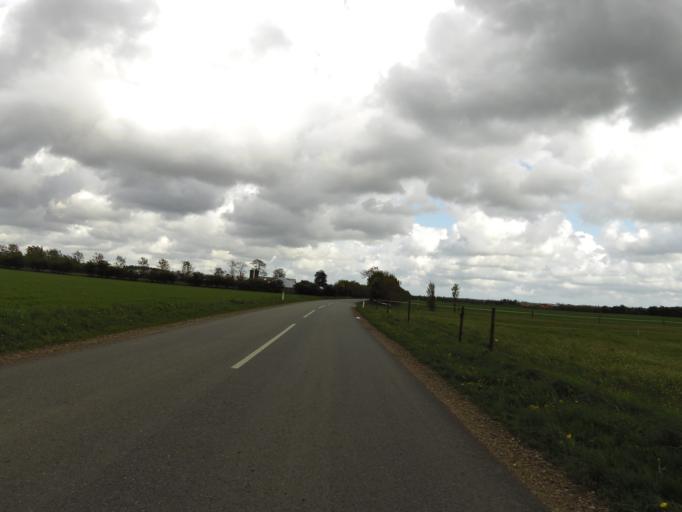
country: DK
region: South Denmark
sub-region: Haderslev Kommune
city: Gram
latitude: 55.3106
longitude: 8.9920
